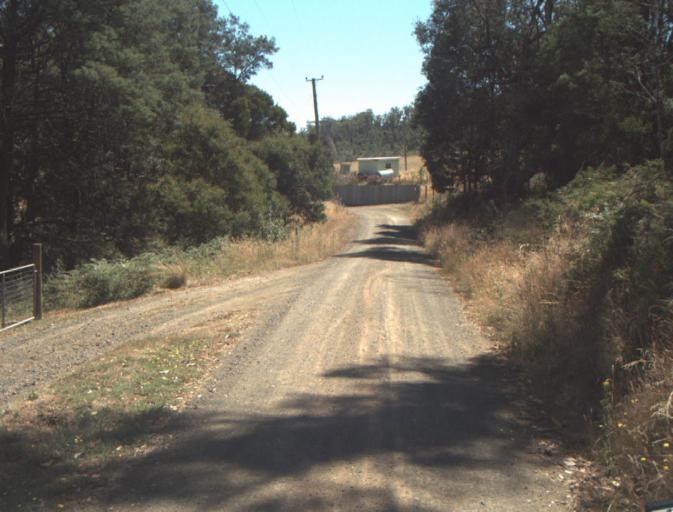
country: AU
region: Tasmania
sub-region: Launceston
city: Newstead
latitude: -41.3519
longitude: 147.3789
